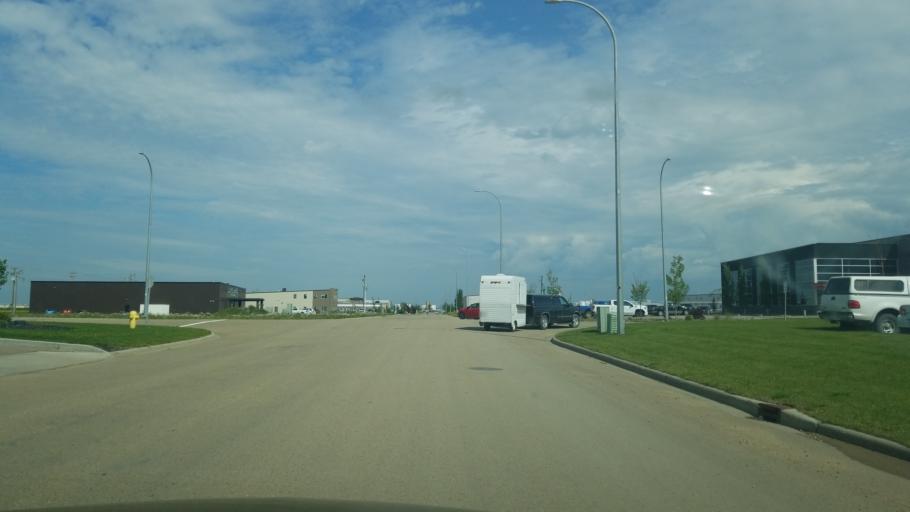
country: CA
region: Saskatchewan
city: Lloydminster
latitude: 53.2915
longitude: -110.0476
